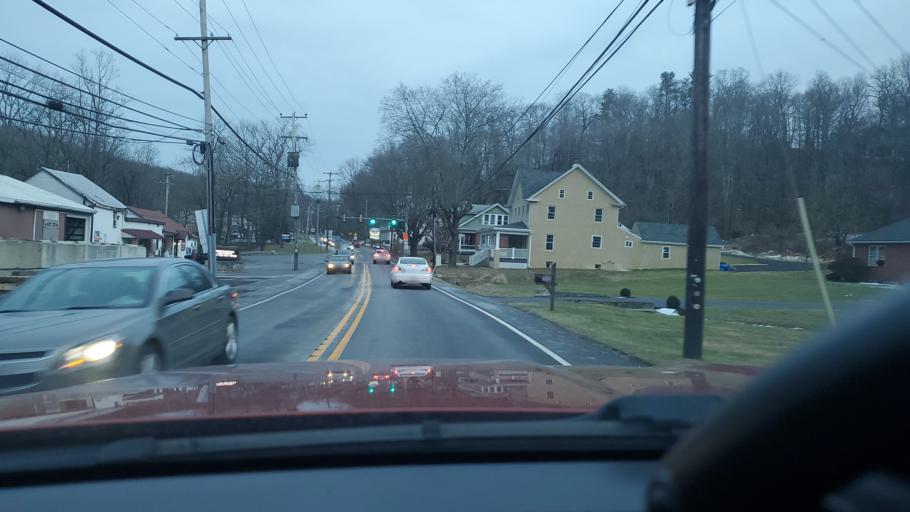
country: US
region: Pennsylvania
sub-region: Montgomery County
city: Schwenksville
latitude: 40.2690
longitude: -75.4702
